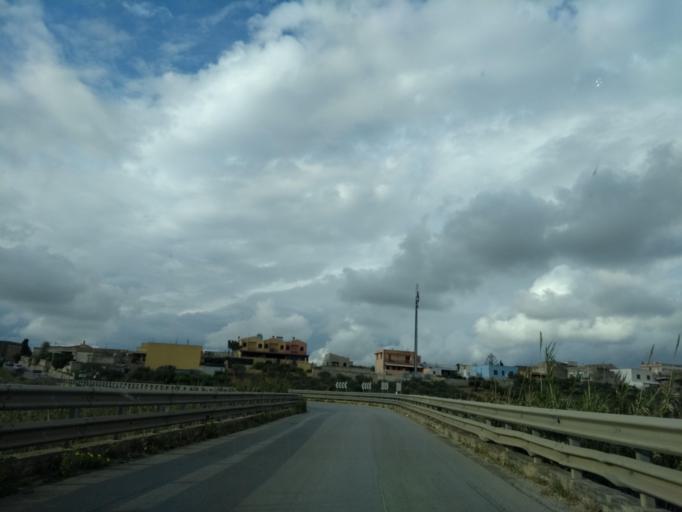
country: IT
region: Sicily
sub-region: Trapani
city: Marausa
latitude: 37.9482
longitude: 12.5142
